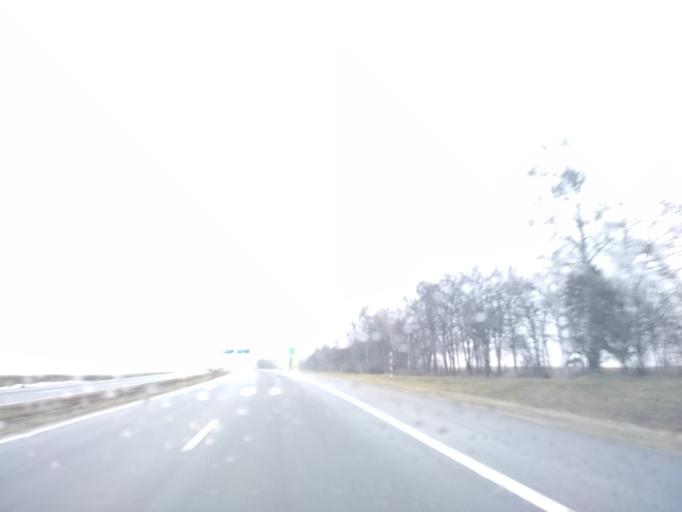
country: BY
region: Minsk
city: Blon'
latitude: 53.5513
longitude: 28.1594
